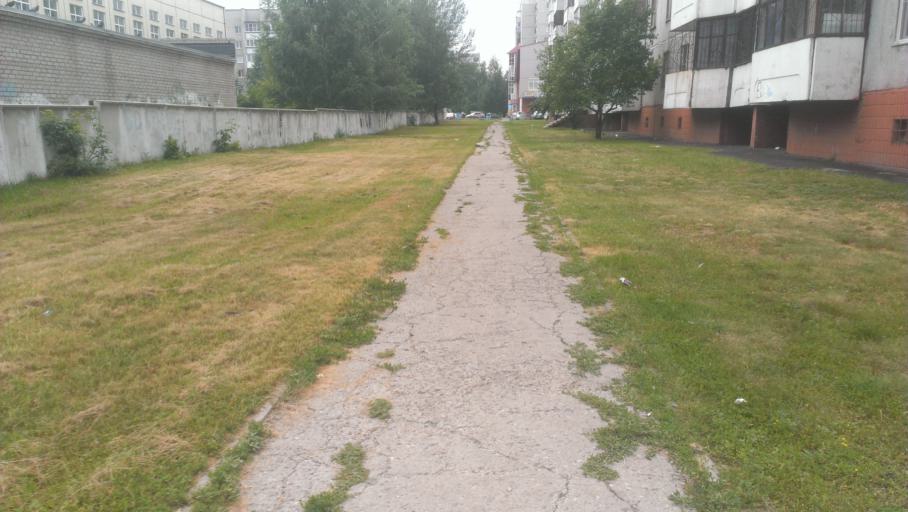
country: RU
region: Altai Krai
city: Novosilikatnyy
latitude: 53.3332
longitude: 83.6819
